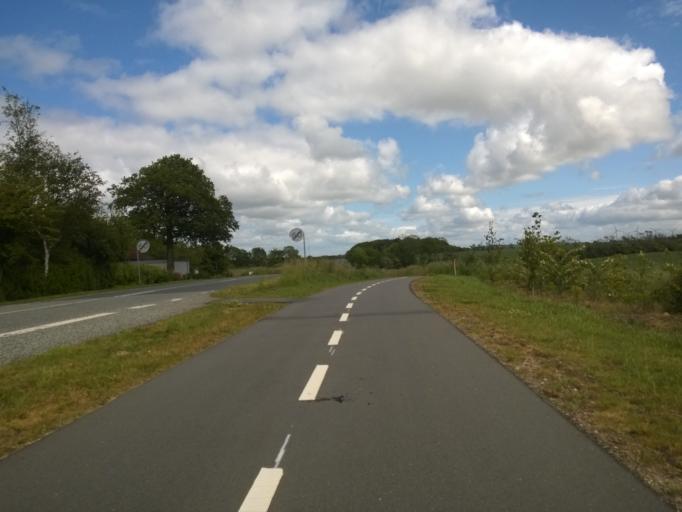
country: DK
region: Central Jutland
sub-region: Holstebro Kommune
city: Vinderup
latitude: 56.4758
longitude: 8.7986
